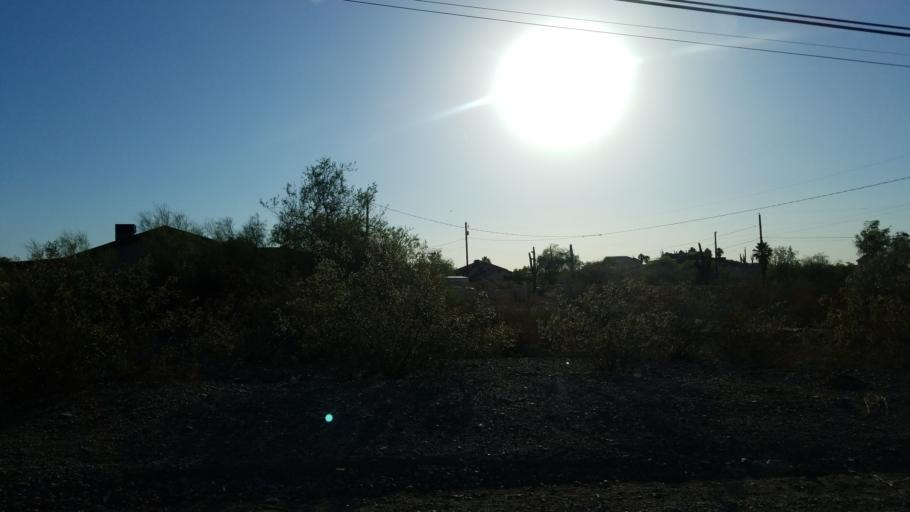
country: US
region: Arizona
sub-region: Maricopa County
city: Laveen
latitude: 33.3558
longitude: -112.1177
